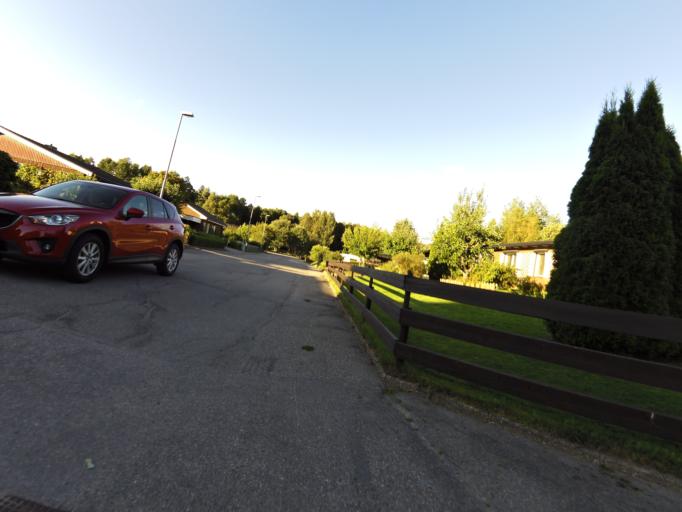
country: SE
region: Gaevleborg
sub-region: Gavle Kommun
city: Gavle
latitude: 60.7146
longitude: 17.1451
